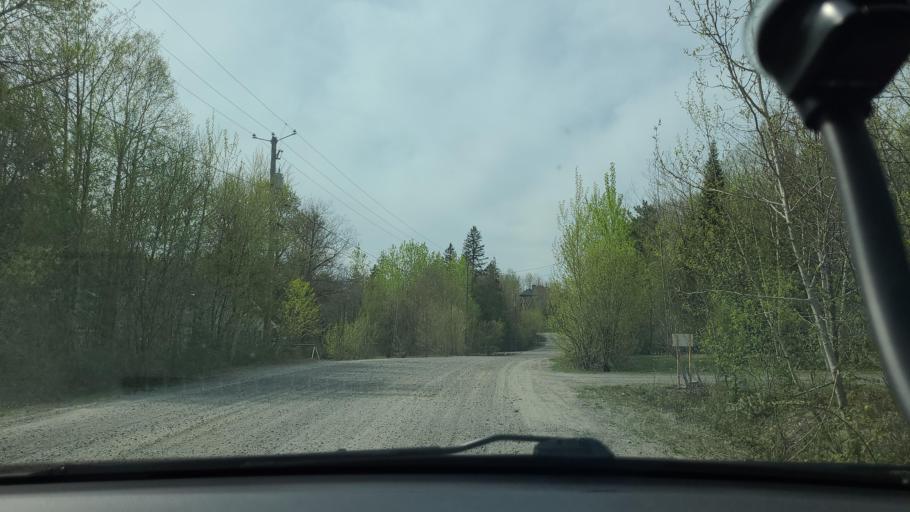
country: CA
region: Quebec
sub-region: Laurentides
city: Prevost
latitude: 45.8971
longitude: -74.0255
